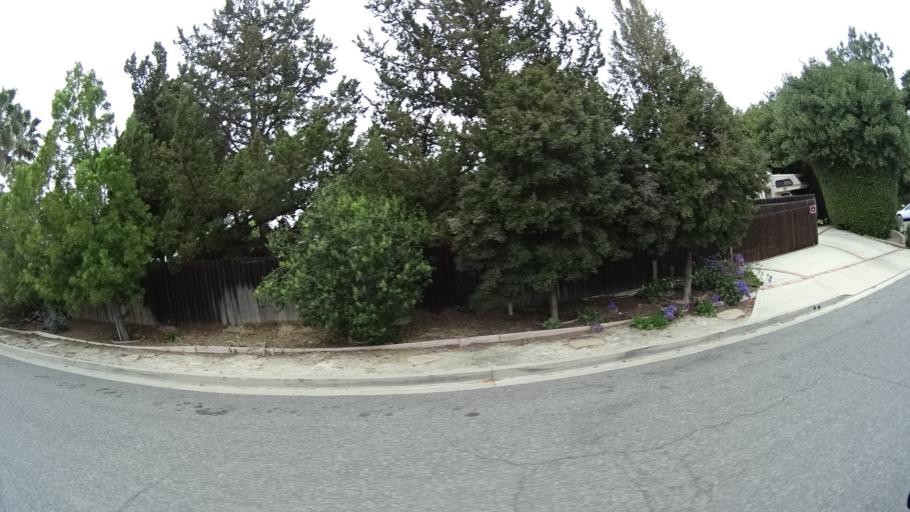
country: US
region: California
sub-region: Ventura County
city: Thousand Oaks
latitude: 34.2049
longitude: -118.8631
